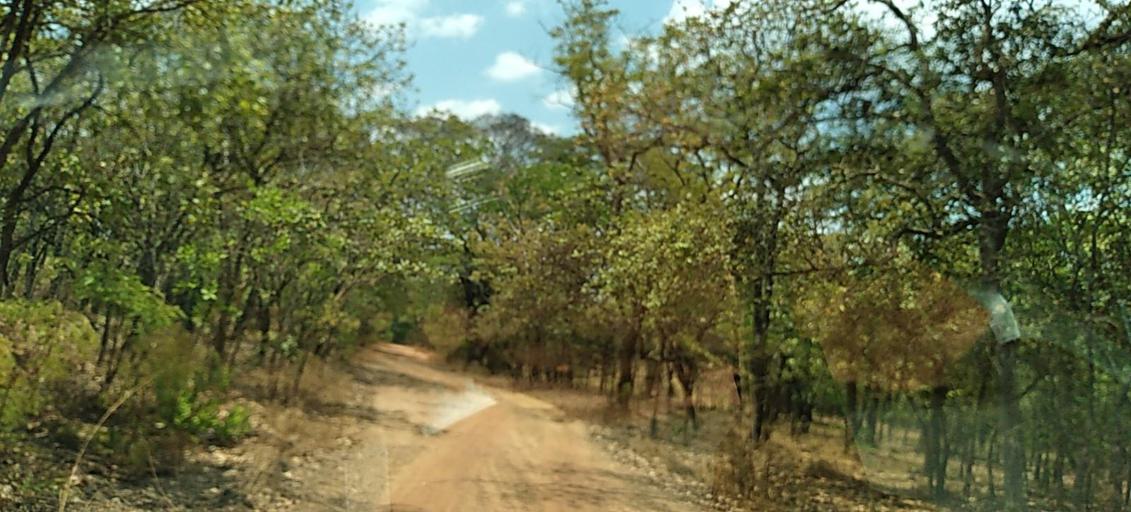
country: ZM
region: Copperbelt
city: Chililabombwe
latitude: -12.5050
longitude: 27.6356
